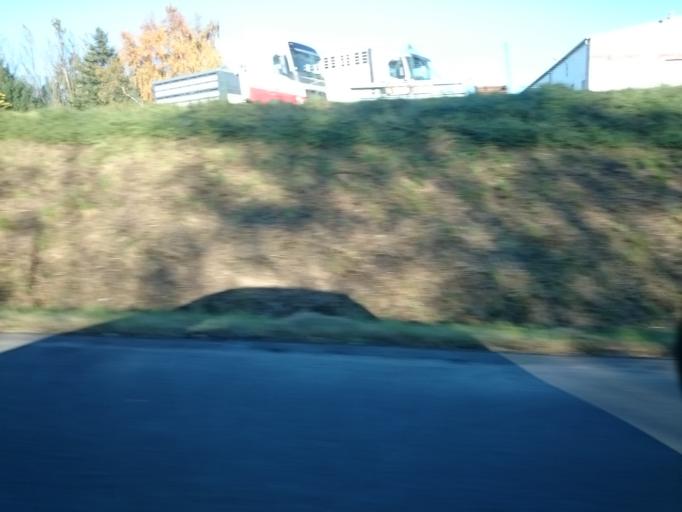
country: FR
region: Brittany
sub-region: Departement des Cotes-d'Armor
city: Broons
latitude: 48.3443
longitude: -2.2880
